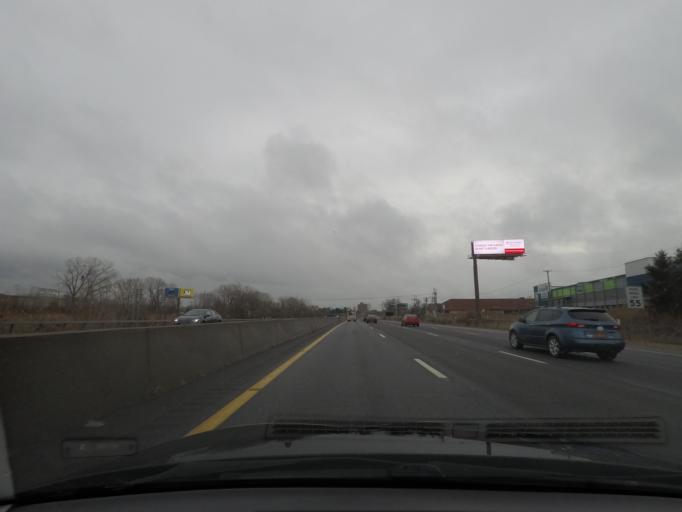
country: US
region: New York
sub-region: Albany County
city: West Albany
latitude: 42.6855
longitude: -73.7908
